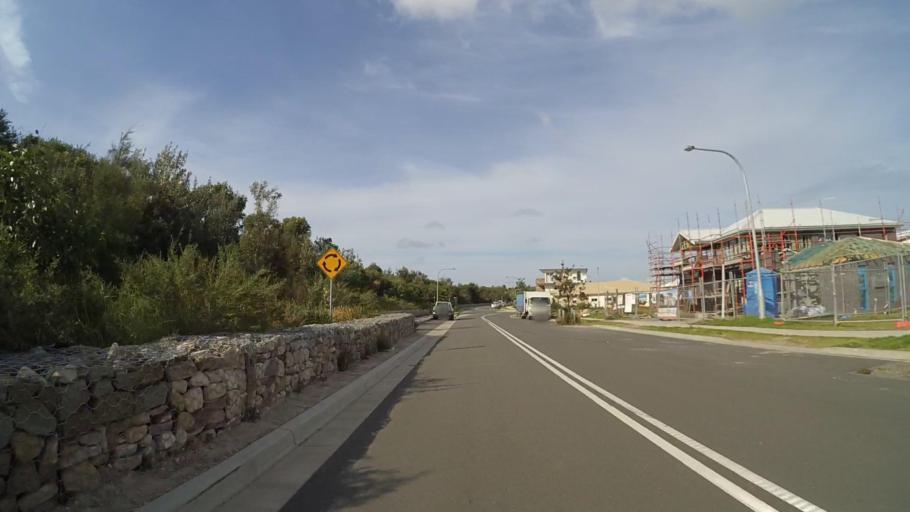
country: AU
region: New South Wales
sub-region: Sutherland Shire
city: Cronulla
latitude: -34.0352
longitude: 151.1668
